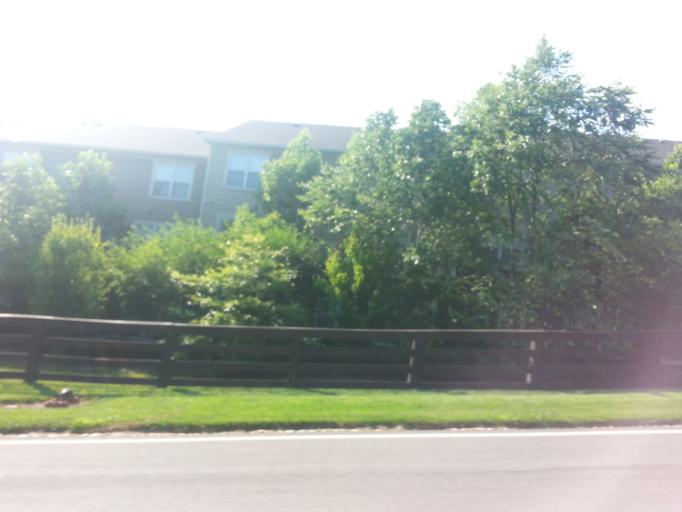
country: US
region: Tennessee
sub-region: Knox County
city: Knoxville
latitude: 35.9365
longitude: -83.9274
